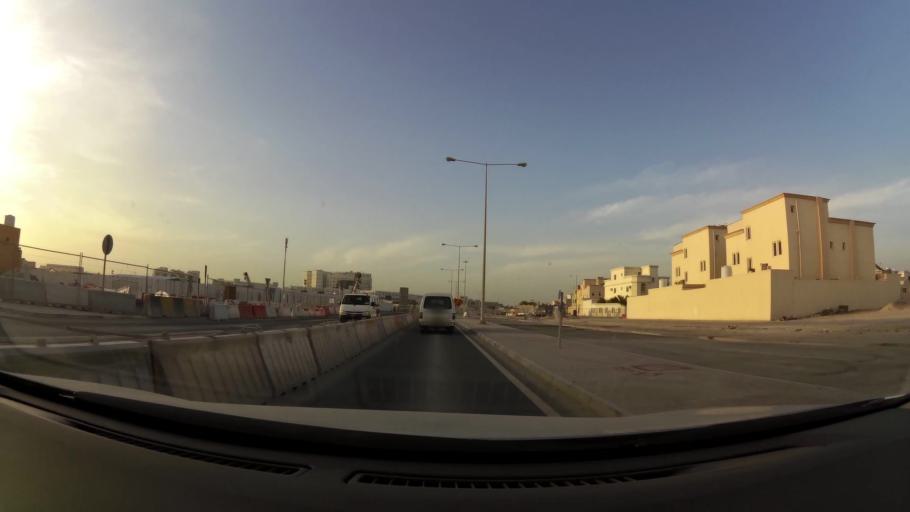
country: QA
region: Al Wakrah
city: Al Wakrah
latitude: 25.1627
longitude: 51.5903
